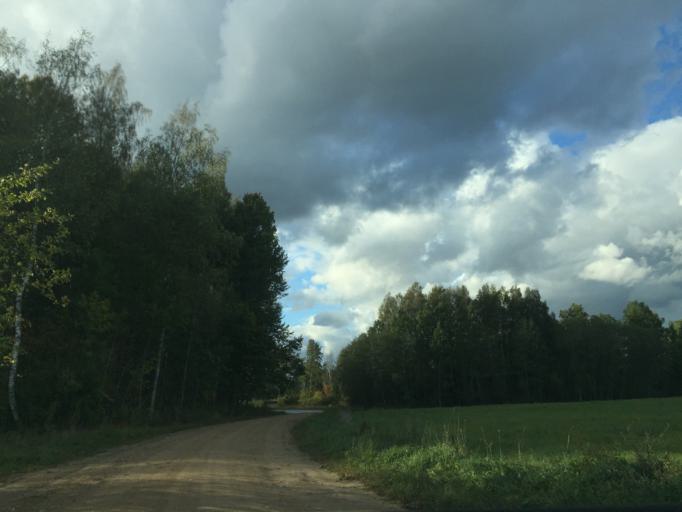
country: LV
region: Ligatne
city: Ligatne
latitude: 57.1381
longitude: 25.0840
